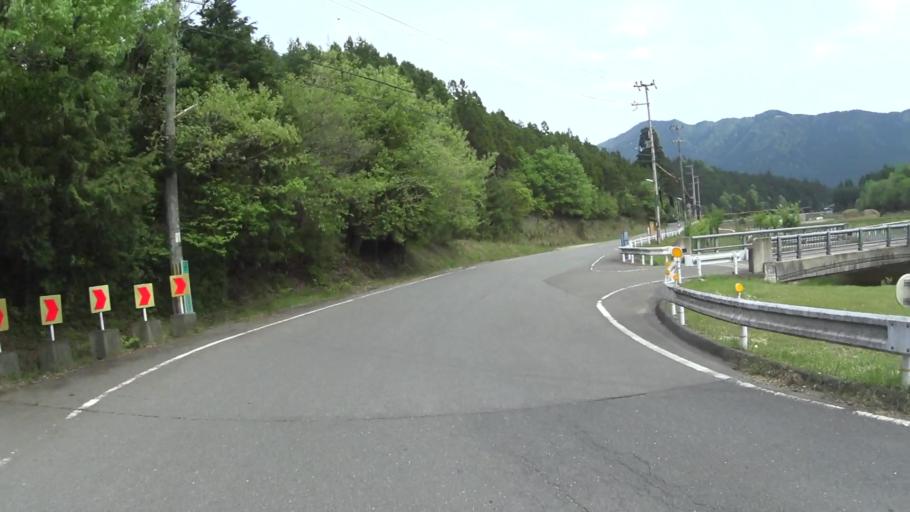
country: JP
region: Kyoto
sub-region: Kyoto-shi
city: Kamigyo-ku
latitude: 35.1863
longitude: 135.6524
